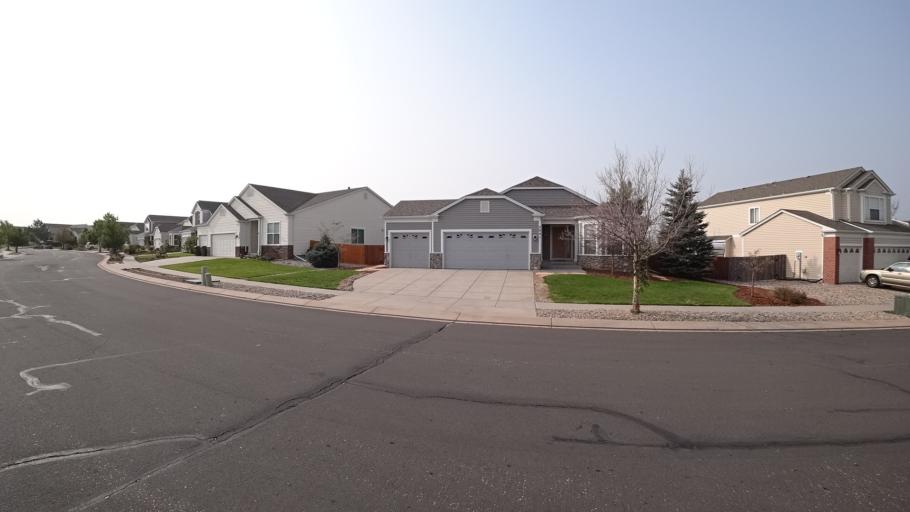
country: US
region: Colorado
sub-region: El Paso County
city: Cimarron Hills
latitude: 38.9316
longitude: -104.7331
